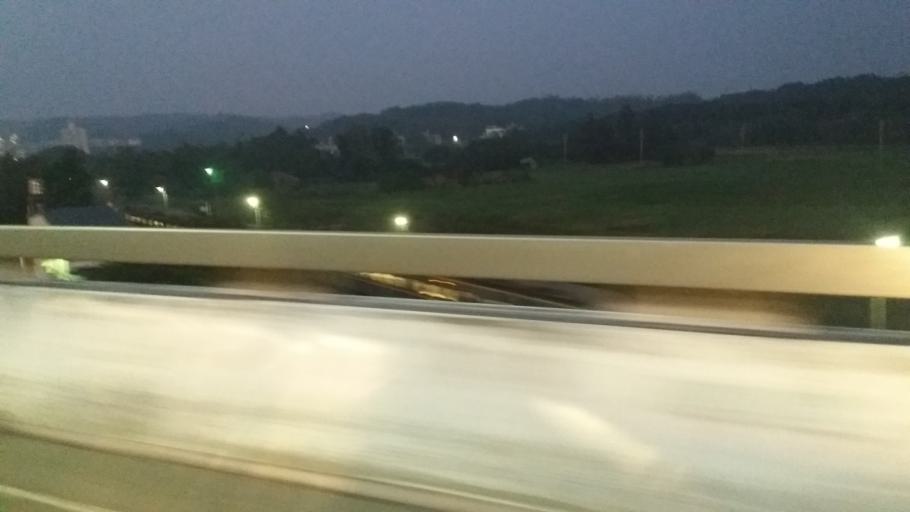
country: TW
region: Taiwan
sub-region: Hsinchu
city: Hsinchu
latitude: 24.7563
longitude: 120.9108
